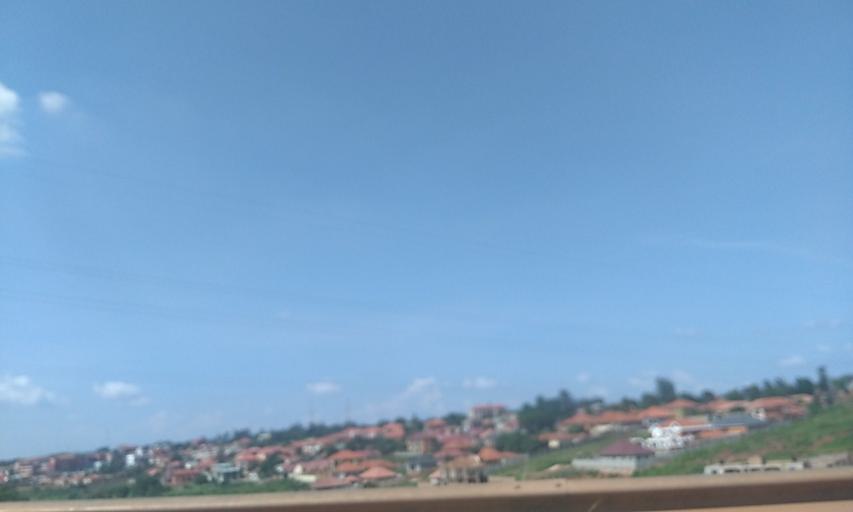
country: UG
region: Central Region
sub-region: Wakiso District
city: Kireka
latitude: 0.3665
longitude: 32.6451
